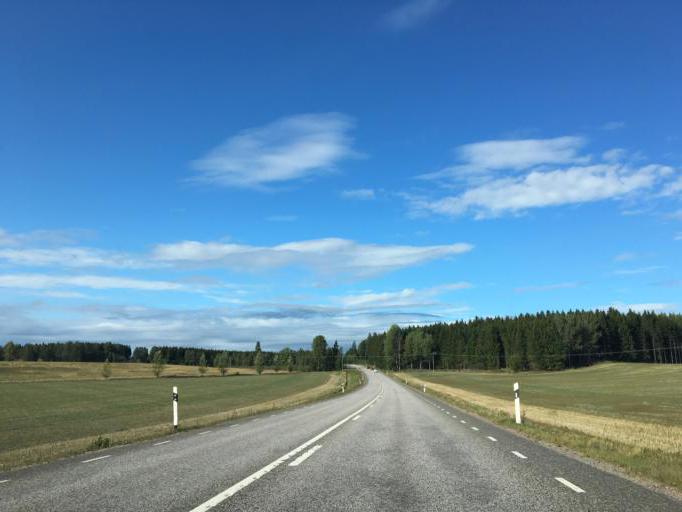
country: SE
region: Soedermanland
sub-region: Nykopings Kommun
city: Svalsta
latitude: 58.8364
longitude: 16.9233
